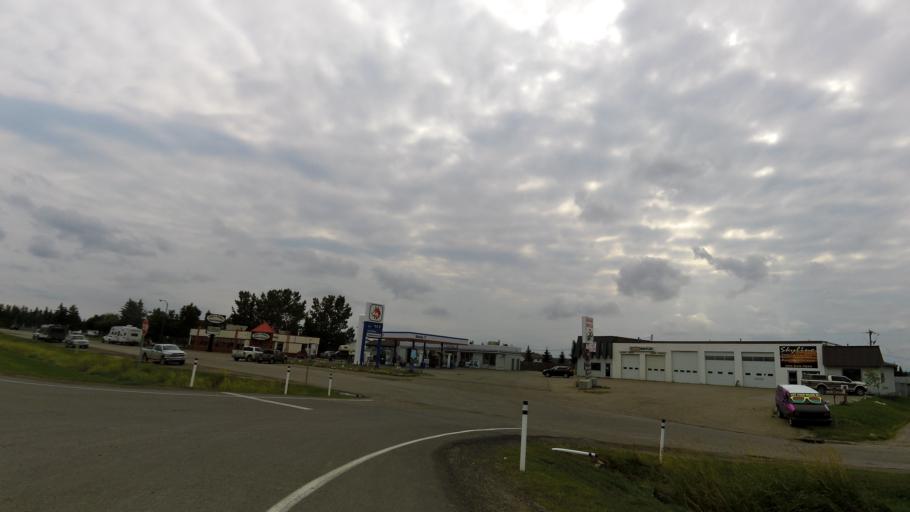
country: CA
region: Alberta
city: Rocky Mountain House
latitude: 52.3690
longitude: -114.9094
